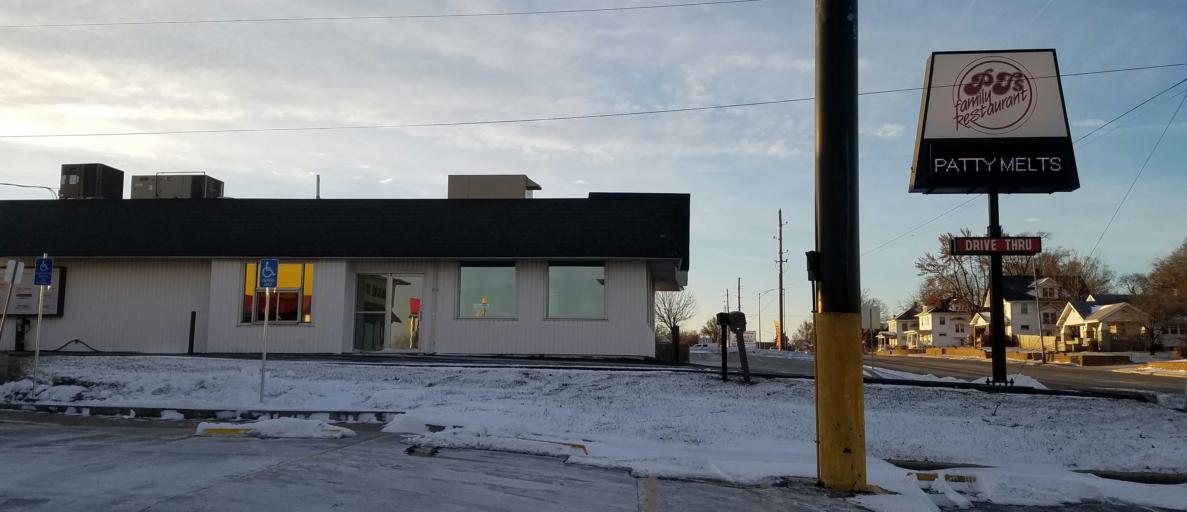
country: US
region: Missouri
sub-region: Jackson County
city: Oak Grove
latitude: 39.0120
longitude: -94.1285
